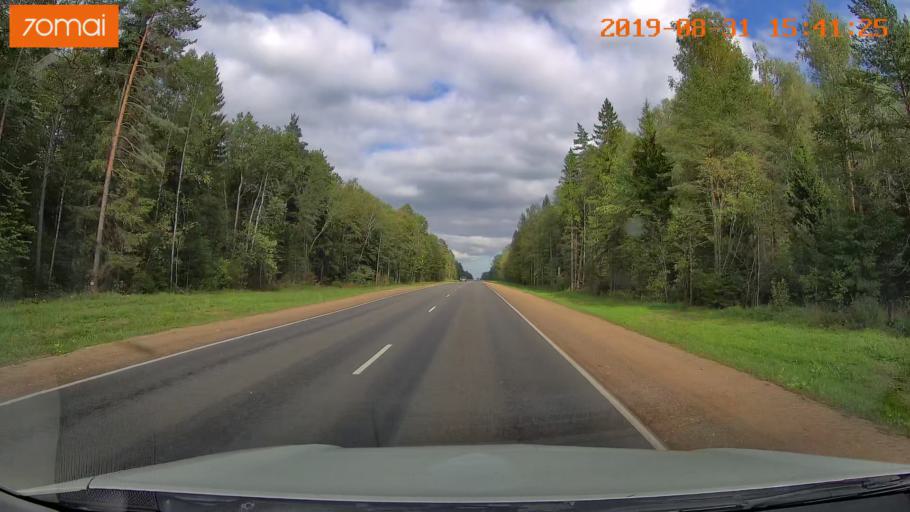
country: RU
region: Kaluga
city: Mosal'sk
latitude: 54.6391
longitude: 34.8600
